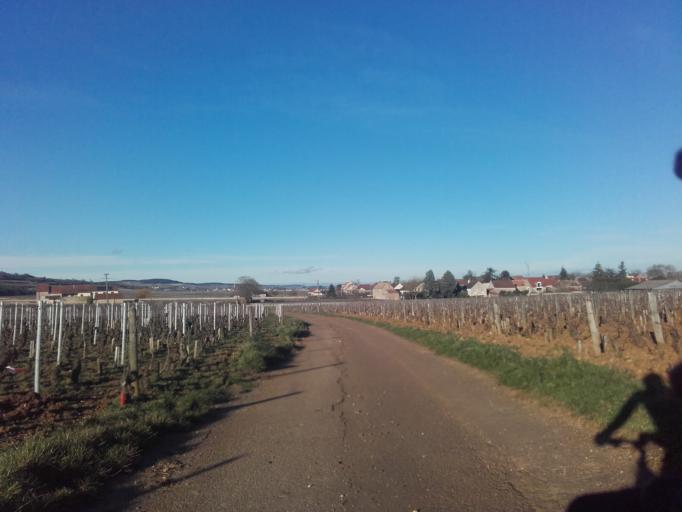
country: FR
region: Bourgogne
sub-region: Departement de la Cote-d'Or
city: Corpeau
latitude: 46.9433
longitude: 4.7464
